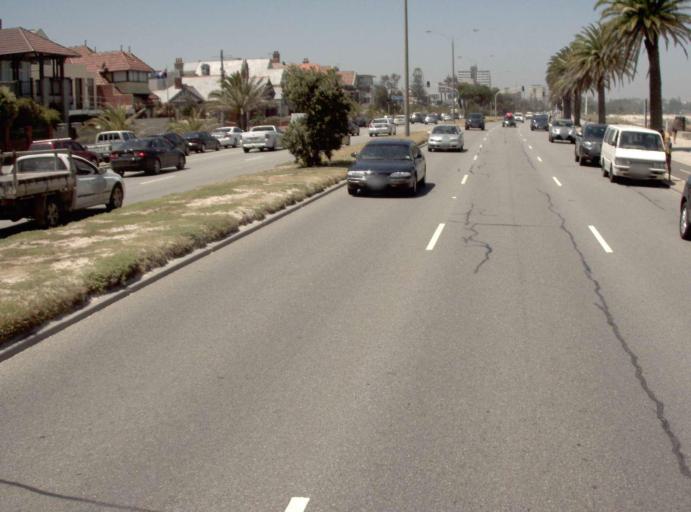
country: AU
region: Victoria
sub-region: Port Phillip
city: Middle Park
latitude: -37.8536
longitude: 144.9604
